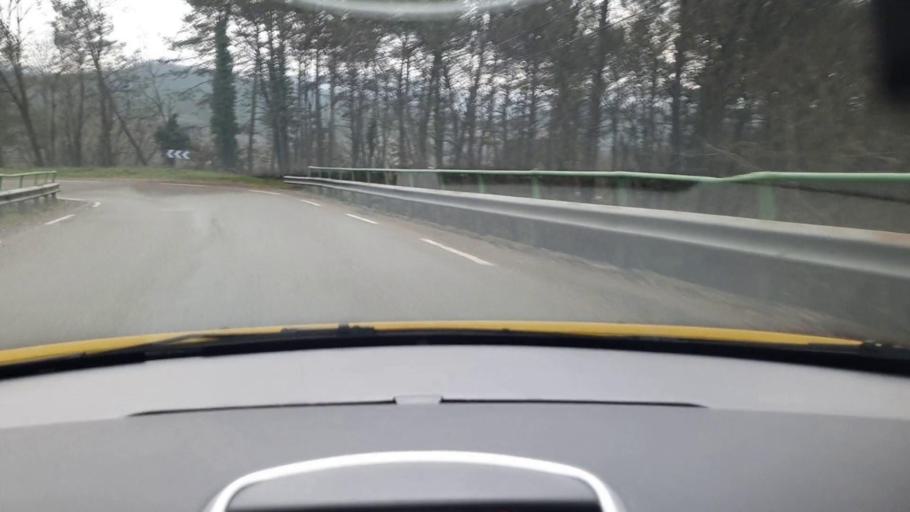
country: FR
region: Languedoc-Roussillon
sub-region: Departement du Gard
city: Besseges
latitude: 44.3169
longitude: 4.1361
